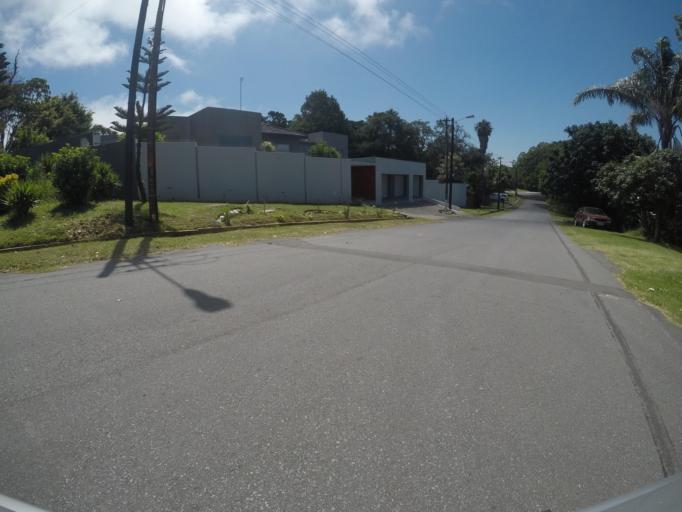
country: ZA
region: Eastern Cape
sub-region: Buffalo City Metropolitan Municipality
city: East London
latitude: -32.9749
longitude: 27.9026
